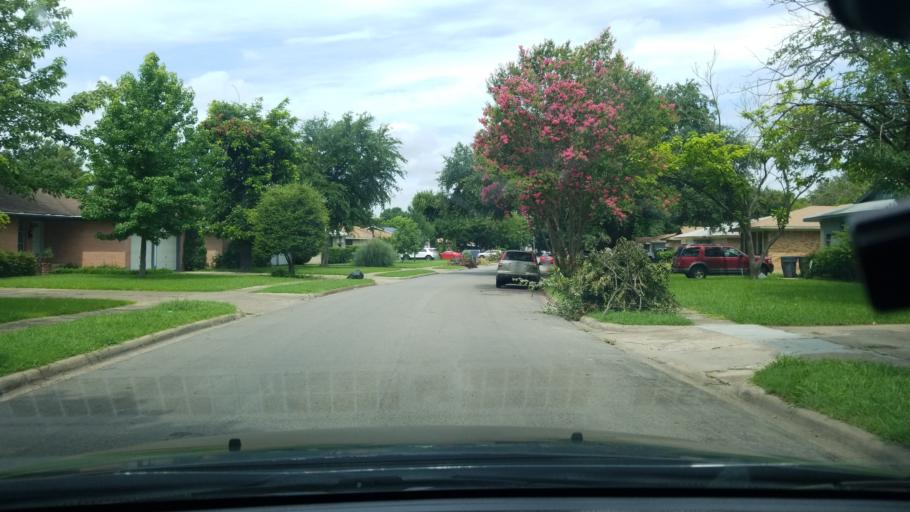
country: US
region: Texas
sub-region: Dallas County
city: Mesquite
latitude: 32.8170
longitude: -96.6746
